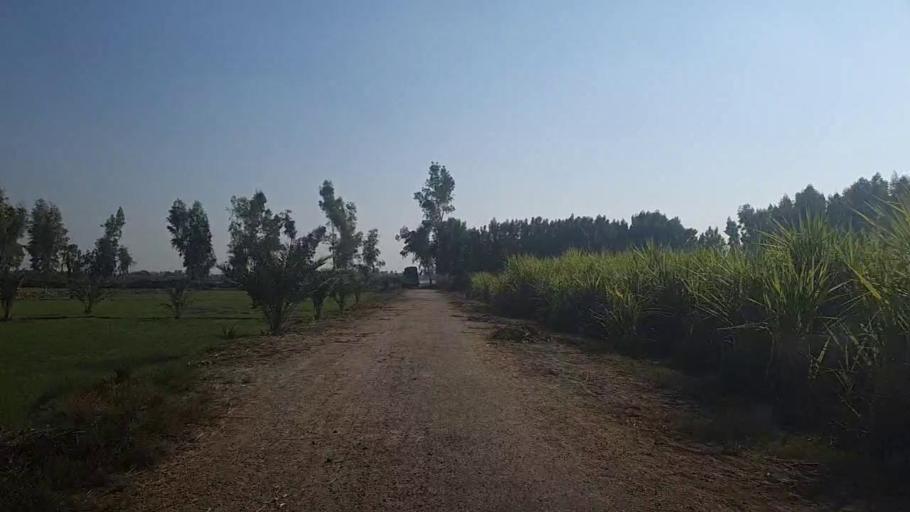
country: PK
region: Sindh
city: Kot Diji
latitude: 27.4324
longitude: 68.7315
